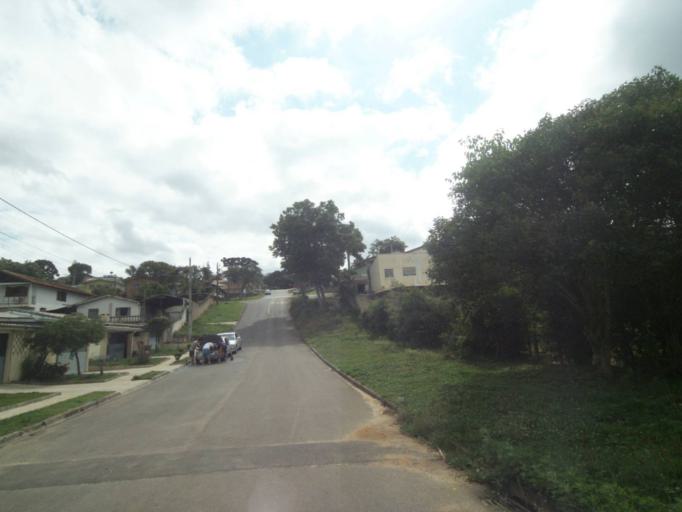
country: BR
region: Parana
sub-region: Curitiba
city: Curitiba
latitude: -25.3779
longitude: -49.2909
